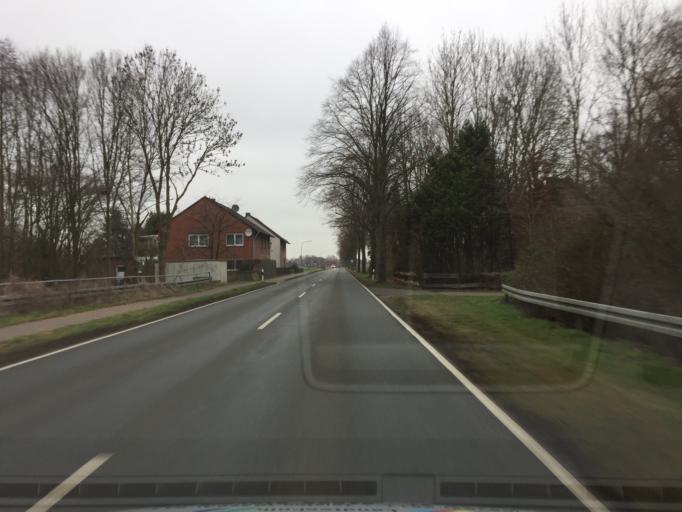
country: DE
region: Lower Saxony
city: Meerbeck
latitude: 52.3335
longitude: 9.1469
